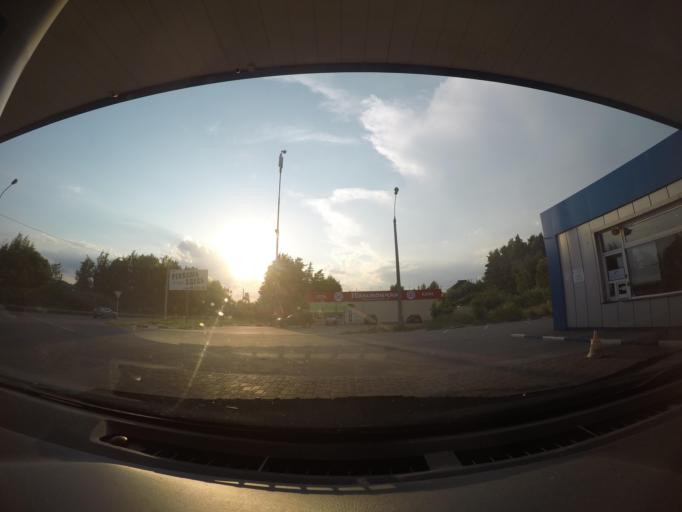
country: RU
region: Moskovskaya
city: Il'inskiy
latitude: 55.6423
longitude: 38.1566
